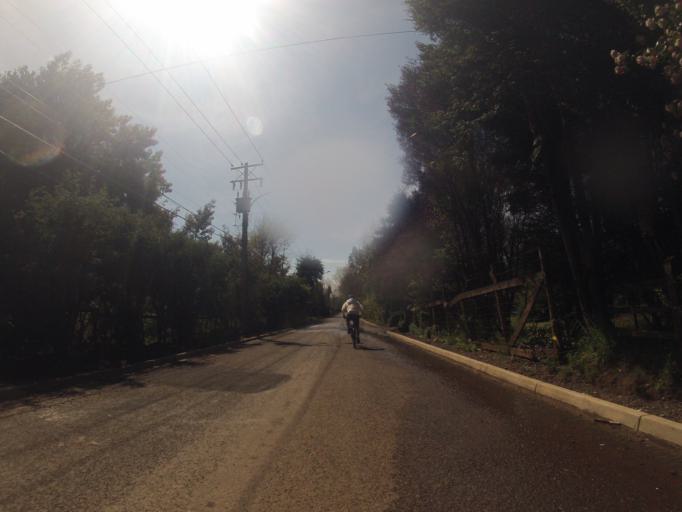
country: CL
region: Araucania
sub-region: Provincia de Cautin
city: Temuco
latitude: -38.6895
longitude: -72.5524
